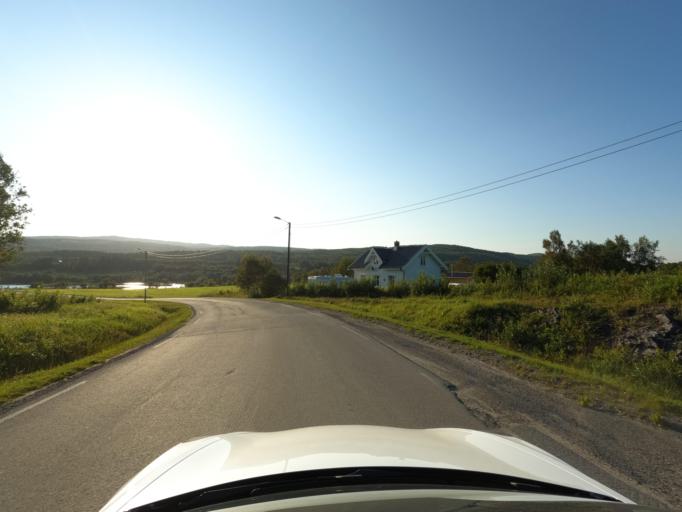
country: NO
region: Troms
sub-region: Skanland
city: Evenskjer
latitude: 68.4653
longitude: 16.6569
